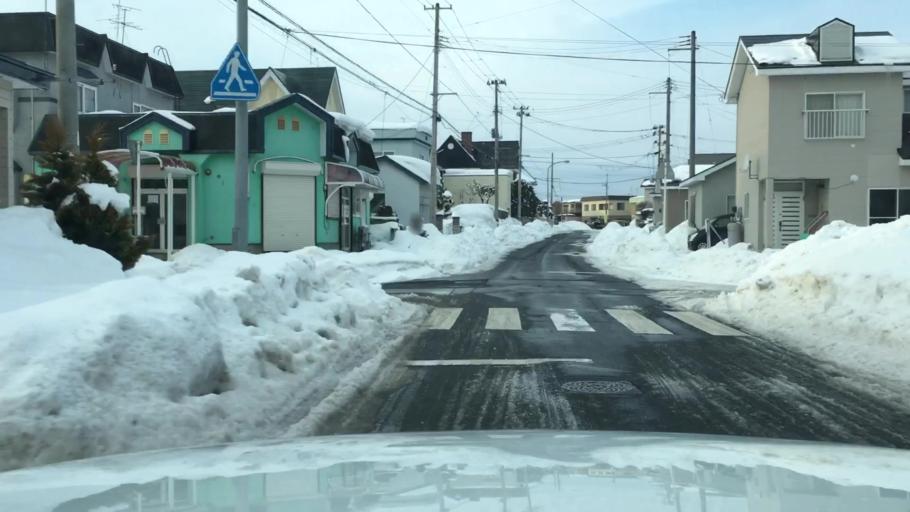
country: JP
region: Aomori
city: Hirosaki
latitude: 40.5775
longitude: 140.4891
